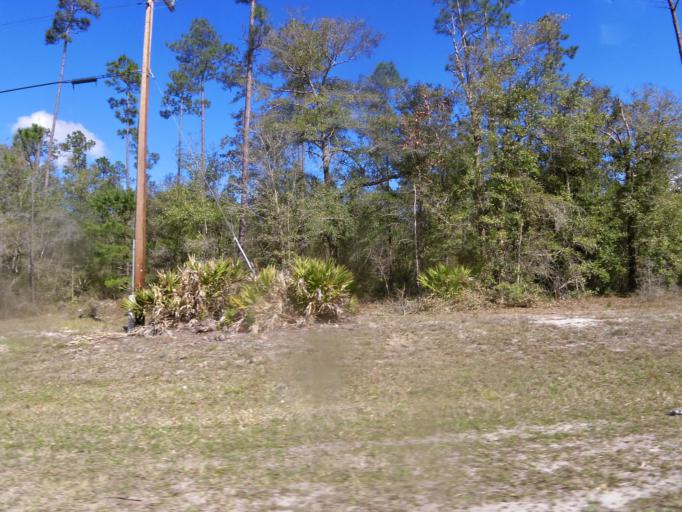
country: US
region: Florida
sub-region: Clay County
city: Green Cove Springs
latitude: 29.8680
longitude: -81.6774
